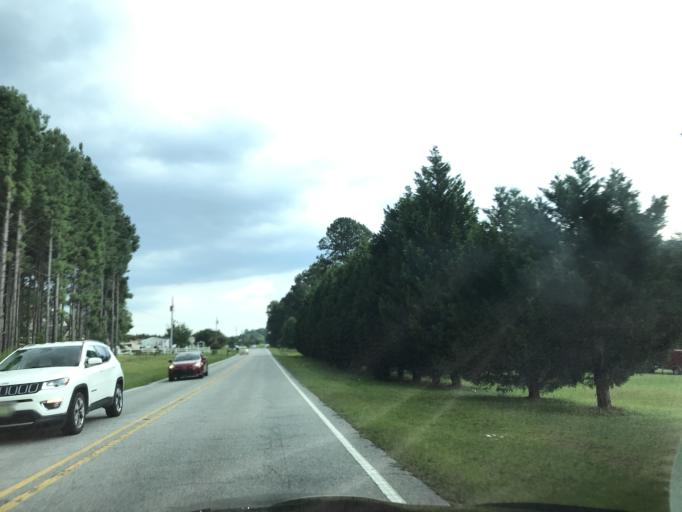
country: US
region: North Carolina
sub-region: Johnston County
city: Four Oaks
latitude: 35.5140
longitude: -78.4898
